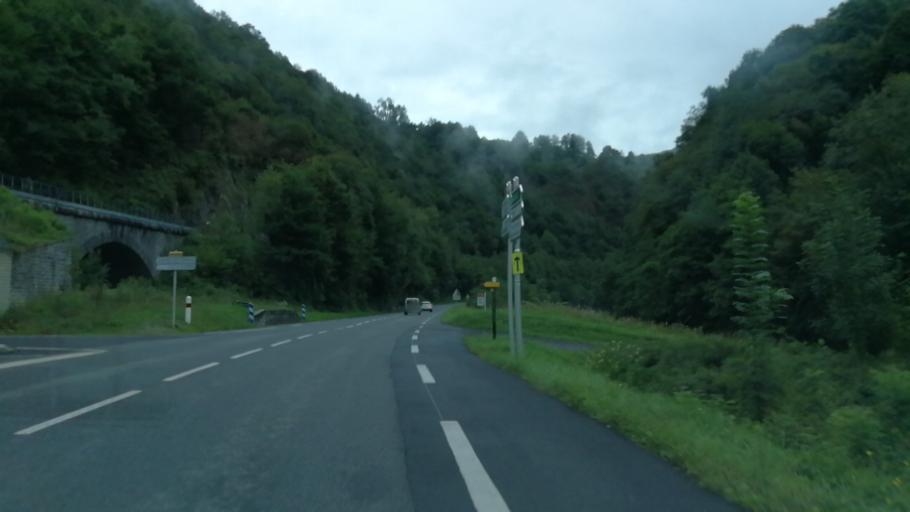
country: FR
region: Aquitaine
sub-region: Departement des Pyrenees-Atlantiques
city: Arette
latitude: 43.0364
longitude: -0.6063
